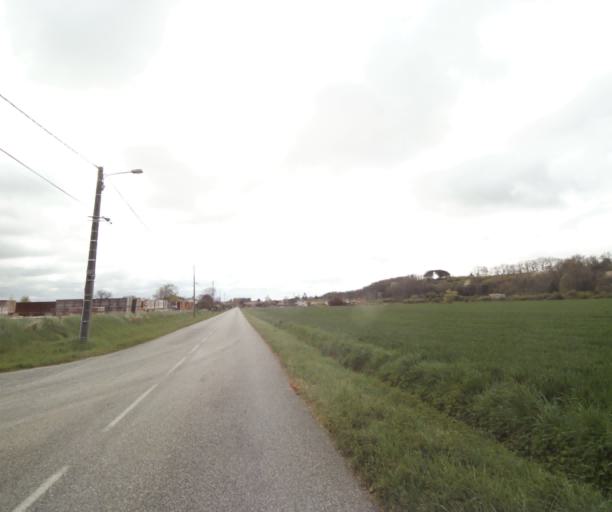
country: FR
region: Midi-Pyrenees
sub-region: Departement de l'Ariege
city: Saverdun
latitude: 43.2451
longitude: 1.5618
